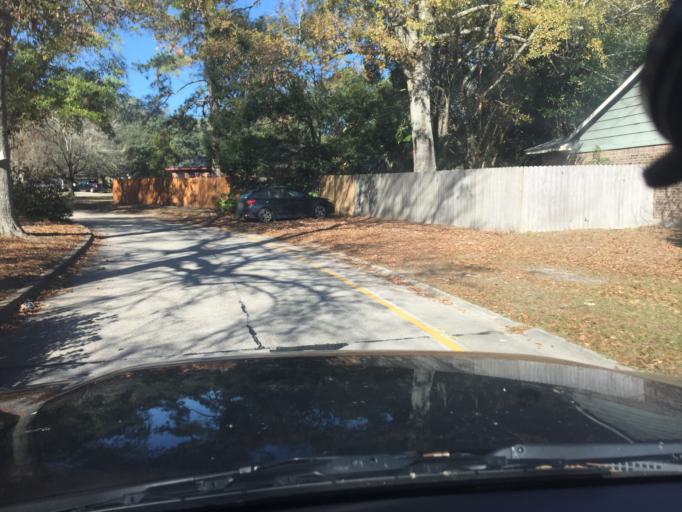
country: US
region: Louisiana
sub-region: Saint Tammany Parish
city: Slidell
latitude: 30.3007
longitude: -89.7256
